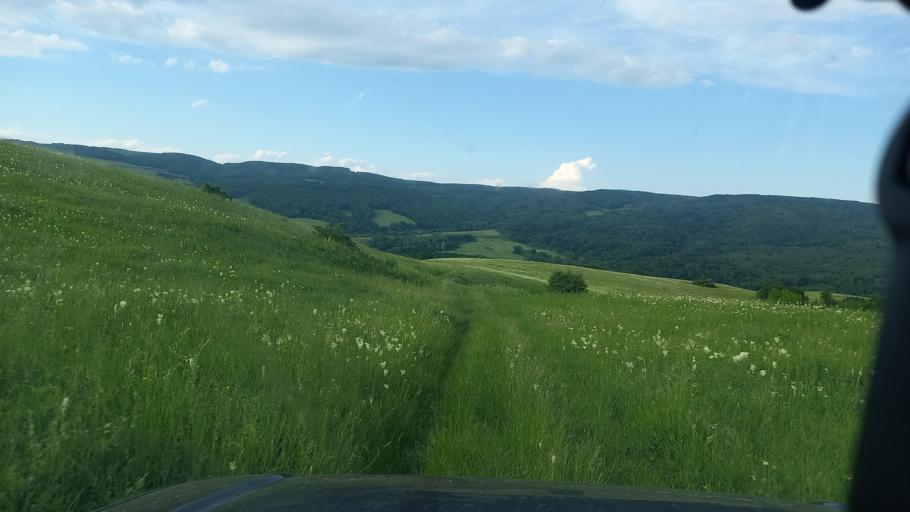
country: RU
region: Karachayevo-Cherkesiya
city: Kurdzhinovo
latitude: 44.1259
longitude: 41.0880
